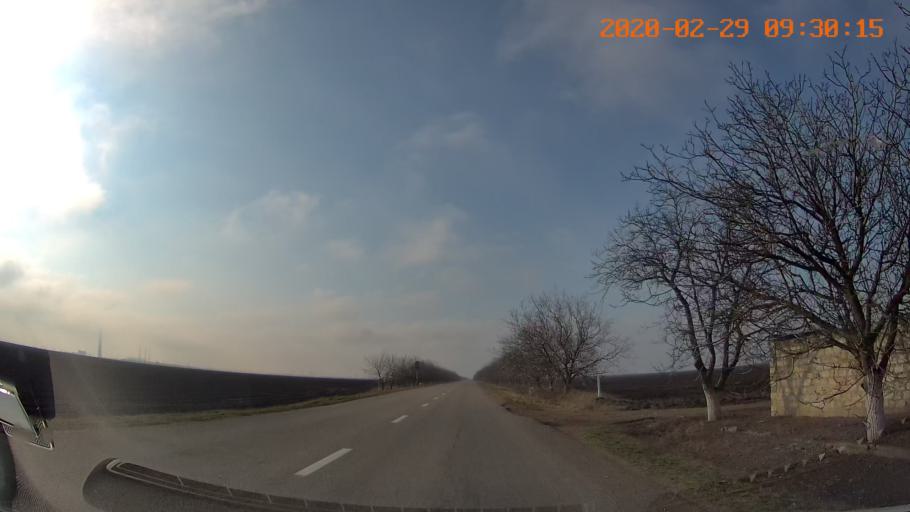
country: UA
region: Odessa
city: Lymanske
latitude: 46.6687
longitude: 29.9174
